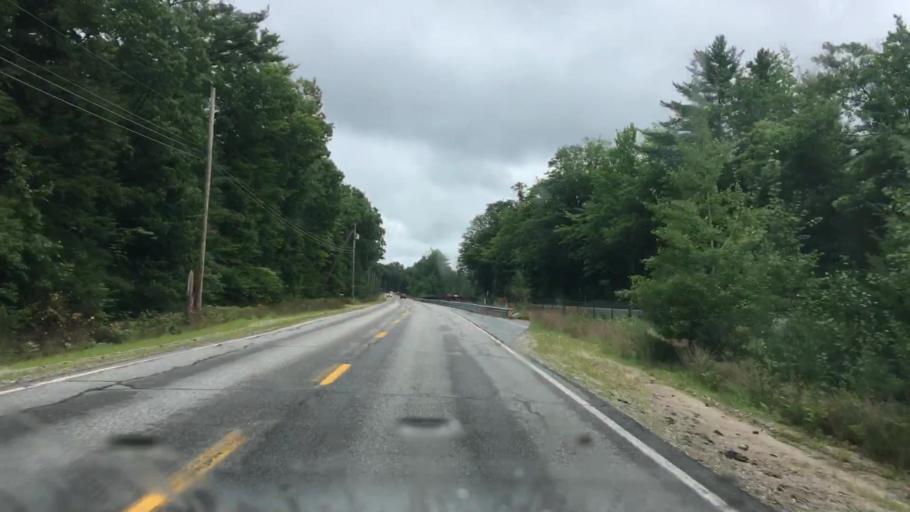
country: US
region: Maine
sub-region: Oxford County
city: Fryeburg
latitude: 44.0074
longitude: -70.9535
